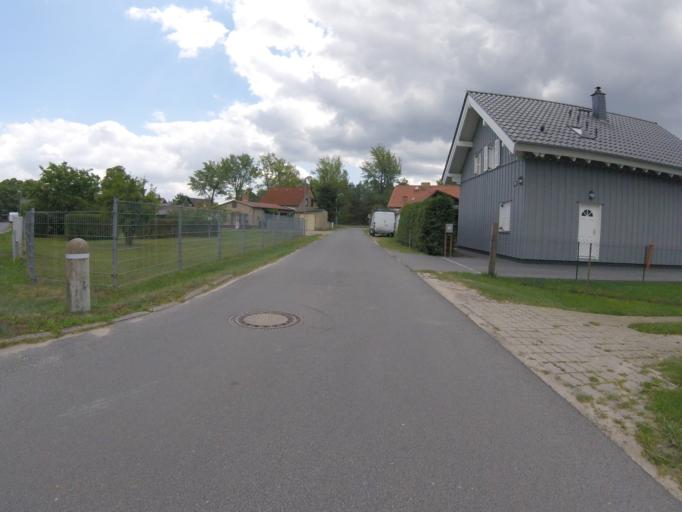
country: DE
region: Brandenburg
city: Bestensee
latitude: 52.2338
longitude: 13.6234
